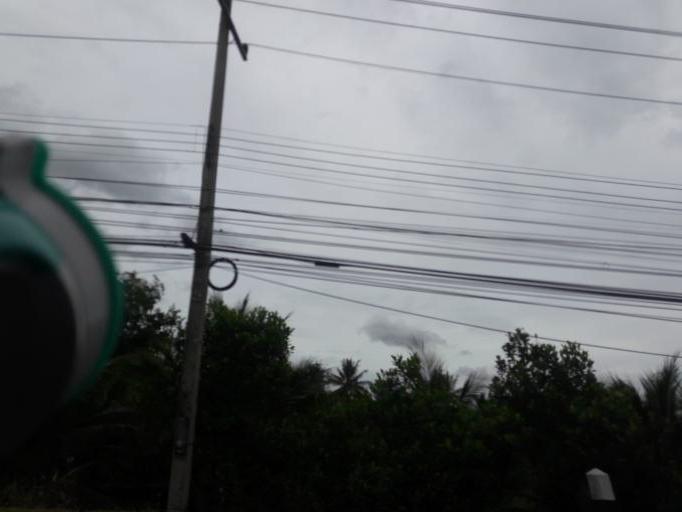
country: TH
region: Ratchaburi
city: Damnoen Saduak
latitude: 13.5202
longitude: 99.9723
